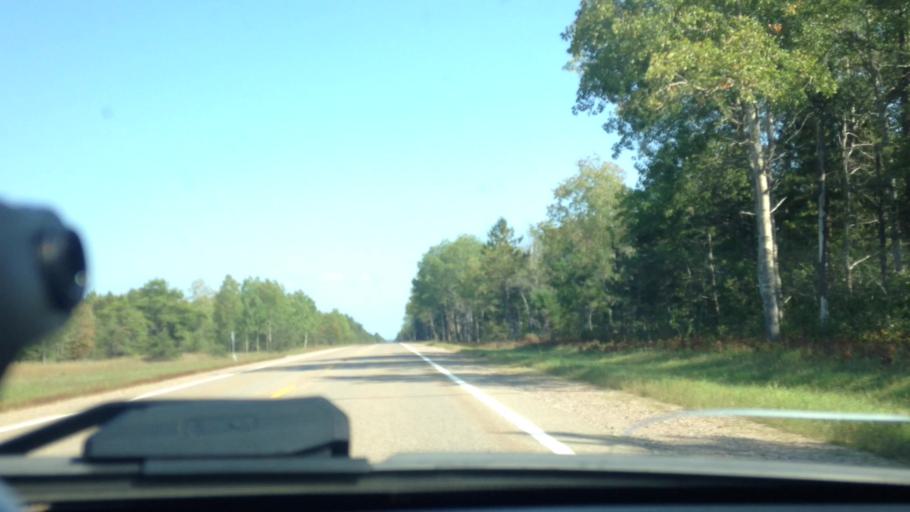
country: US
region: Michigan
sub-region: Mackinac County
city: Saint Ignace
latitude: 46.3584
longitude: -84.8607
